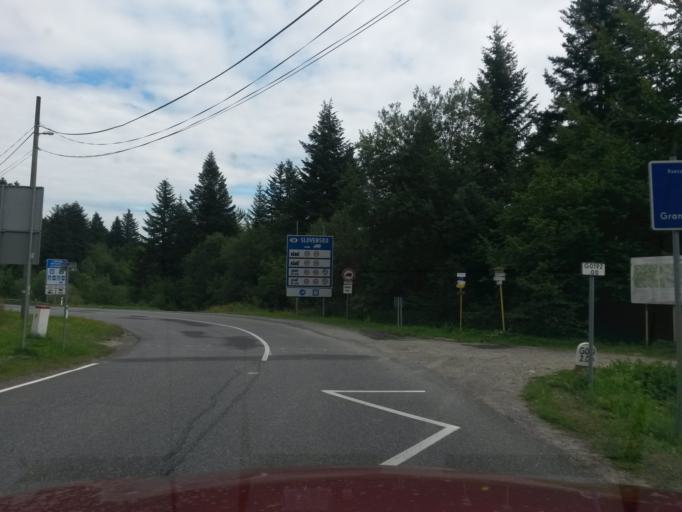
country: PL
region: Lesser Poland Voivodeship
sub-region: Powiat nowosadecki
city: Tylicz
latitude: 49.3745
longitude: 21.1023
